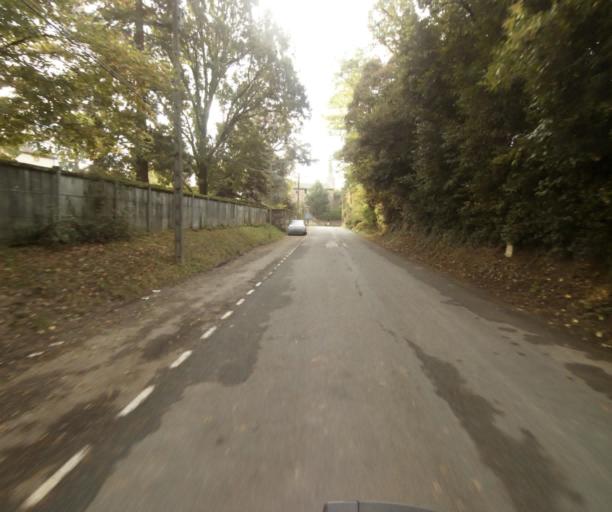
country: FR
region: Midi-Pyrenees
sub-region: Departement du Tarn-et-Garonne
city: Montech
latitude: 43.9594
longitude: 1.2298
